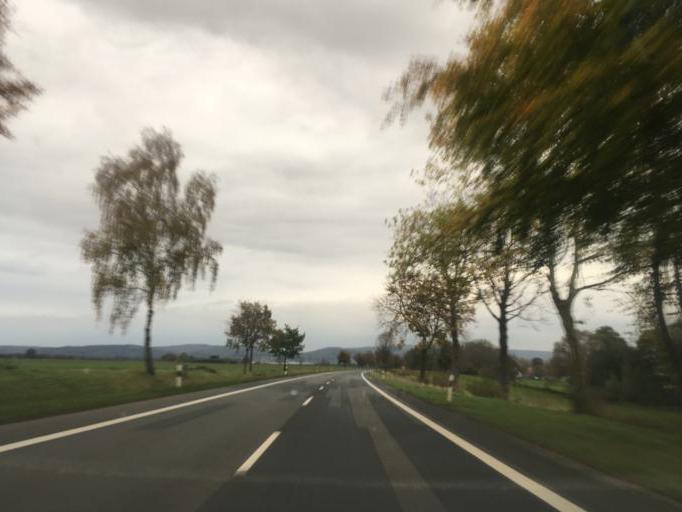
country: DE
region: Lower Saxony
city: Hardegsen
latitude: 51.6402
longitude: 9.8791
